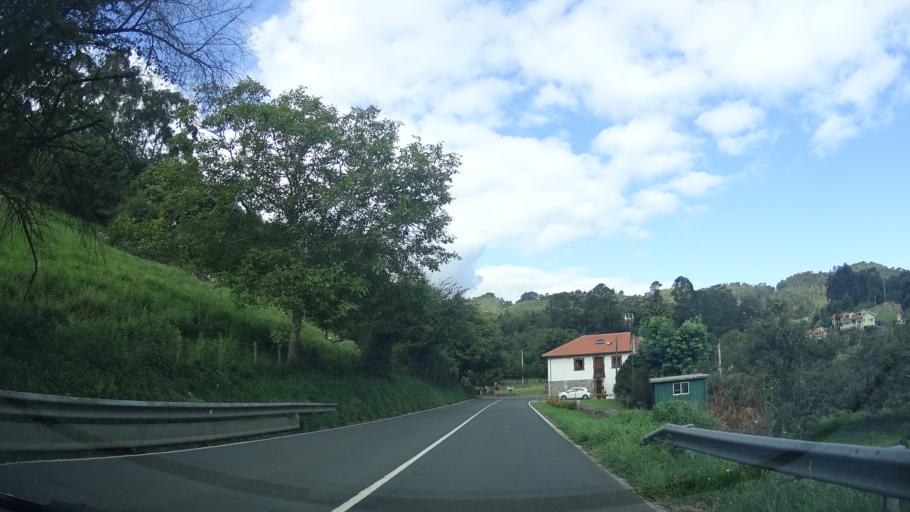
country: ES
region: Asturias
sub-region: Province of Asturias
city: Ribadesella
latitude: 43.4642
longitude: -5.1261
